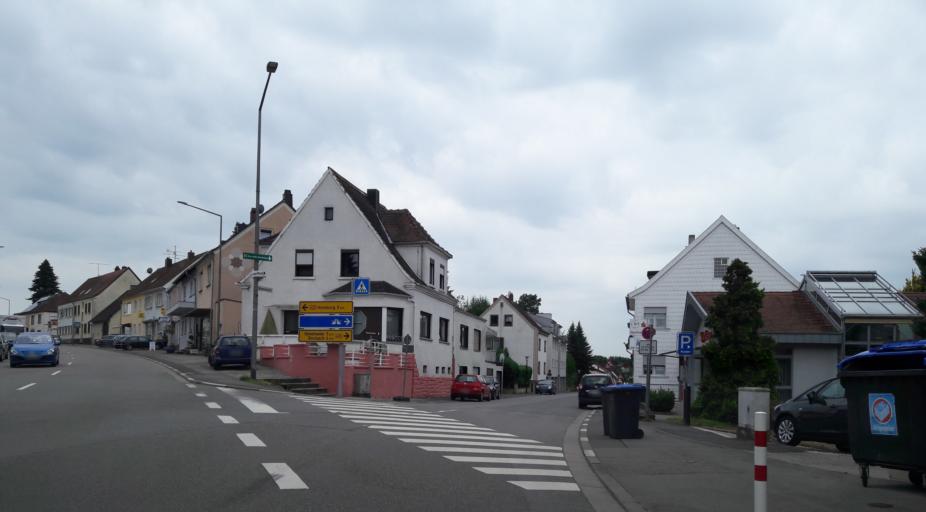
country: DE
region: Rheinland-Pfalz
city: Waldmohr
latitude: 49.3695
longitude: 7.3235
